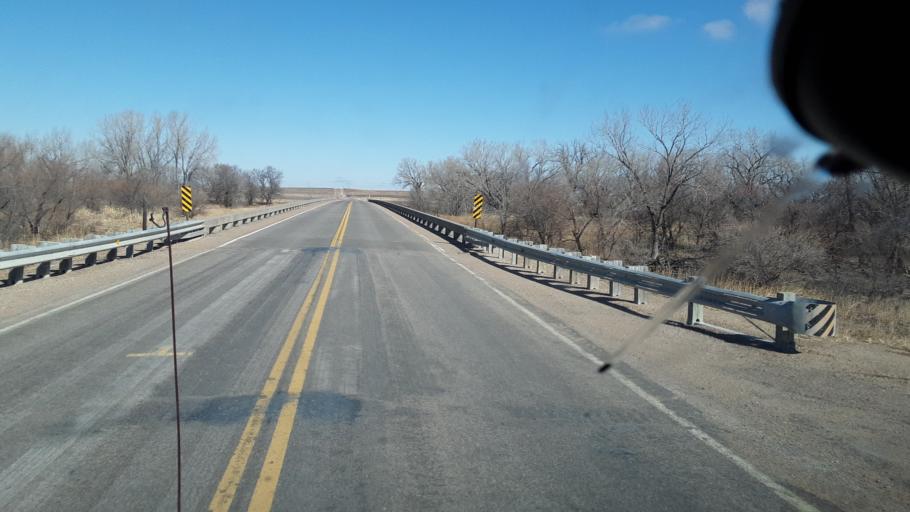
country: US
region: Kansas
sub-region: Barton County
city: Ellinwood
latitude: 38.3552
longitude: -98.6641
